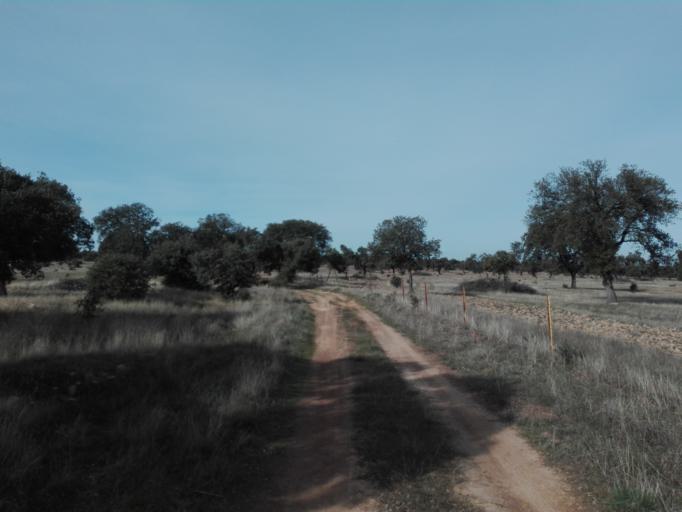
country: ES
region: Extremadura
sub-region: Provincia de Badajoz
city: Campillo de Llerena
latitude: 38.4592
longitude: -5.8760
